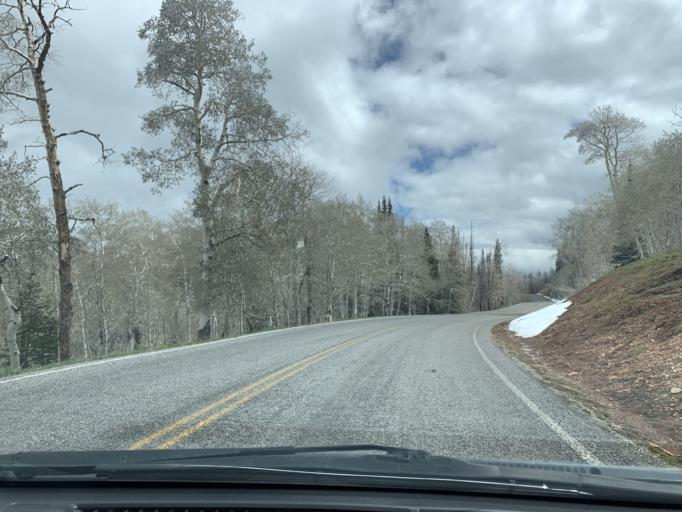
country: US
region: Utah
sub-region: Utah County
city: Santaquin
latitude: 39.8622
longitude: -111.6935
